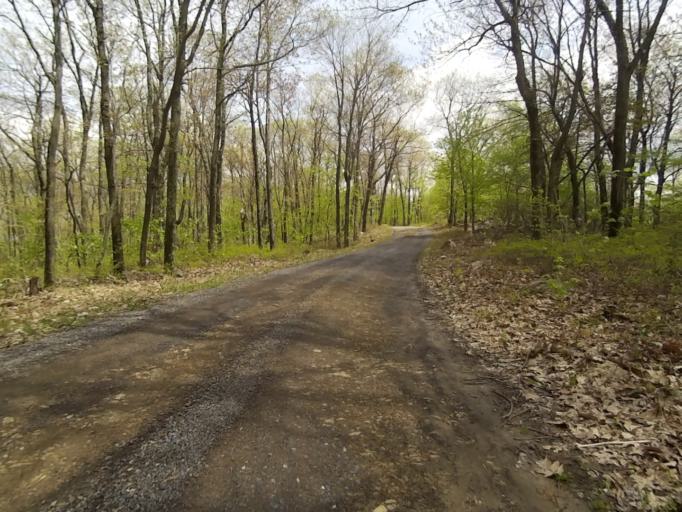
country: US
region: Pennsylvania
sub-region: Centre County
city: Boalsburg
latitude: 40.7494
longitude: -77.7726
